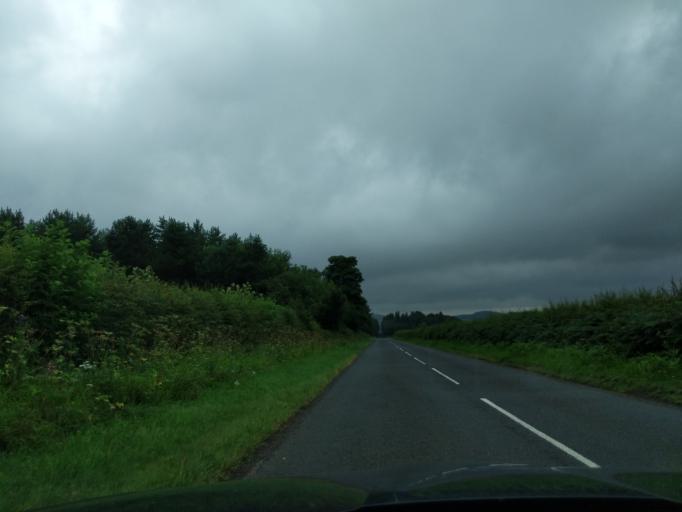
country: GB
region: England
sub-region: Northumberland
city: Ford
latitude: 55.6366
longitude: -2.0726
